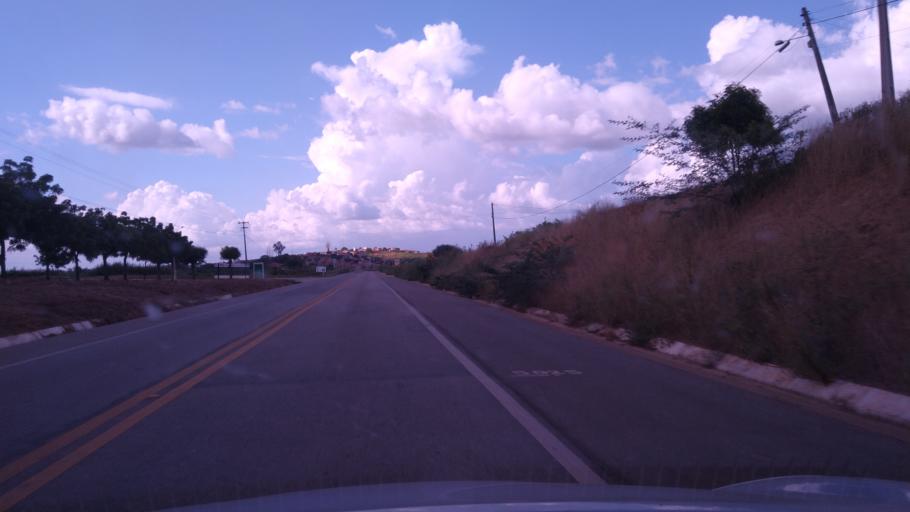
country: BR
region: Ceara
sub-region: Caninde
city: Caninde
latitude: -4.3822
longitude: -39.3107
